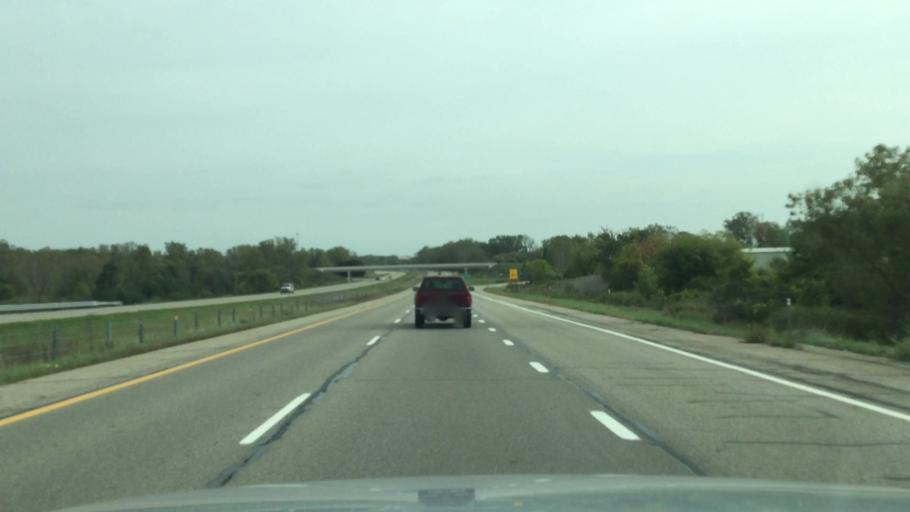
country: US
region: Michigan
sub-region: Shiawassee County
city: Durand
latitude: 42.9255
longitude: -84.0066
